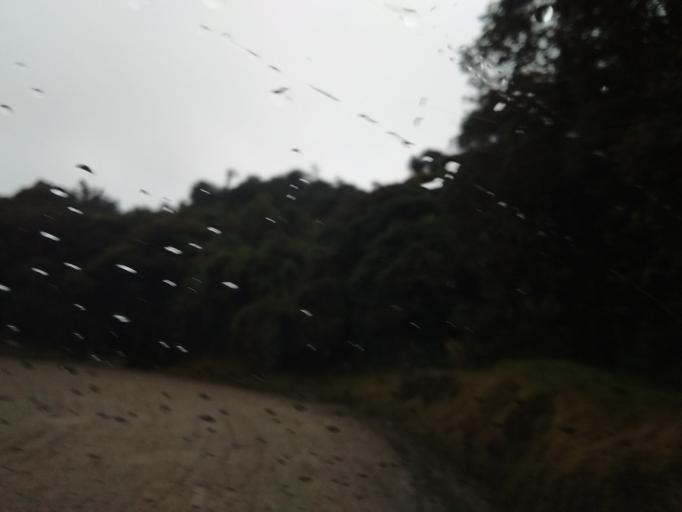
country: CO
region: Cauca
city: Paispamba
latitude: 2.1660
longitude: -76.4030
